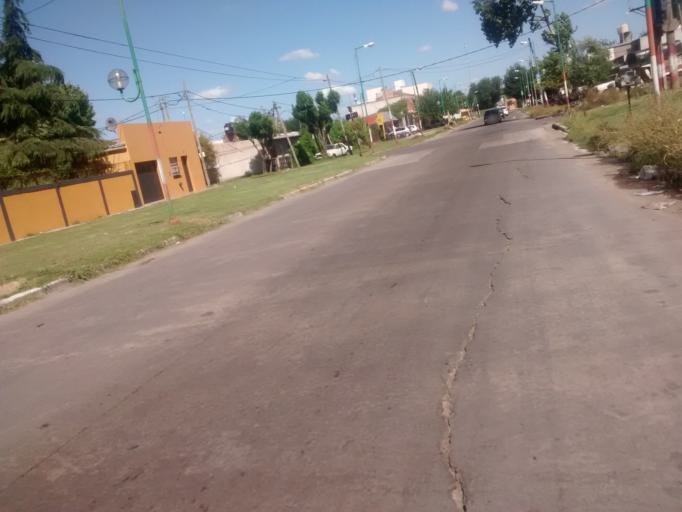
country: AR
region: Buenos Aires
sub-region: Partido de La Plata
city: La Plata
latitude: -34.9283
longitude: -57.9043
